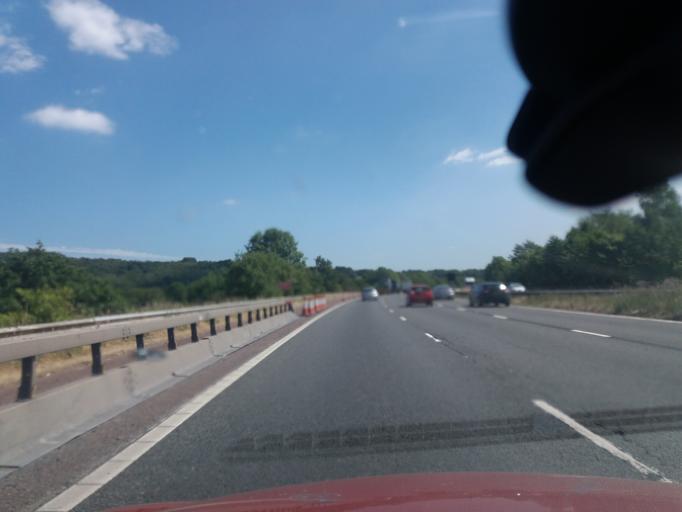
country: GB
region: England
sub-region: Lancashire
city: Chorley
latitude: 53.6622
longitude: -2.6142
